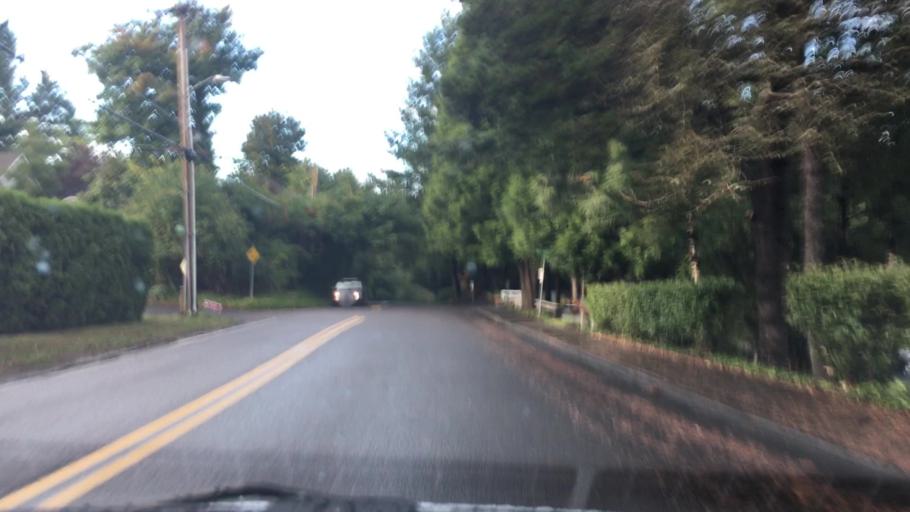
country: US
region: Oregon
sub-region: Washington County
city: Garden Home-Whitford
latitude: 45.4772
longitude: -122.7077
